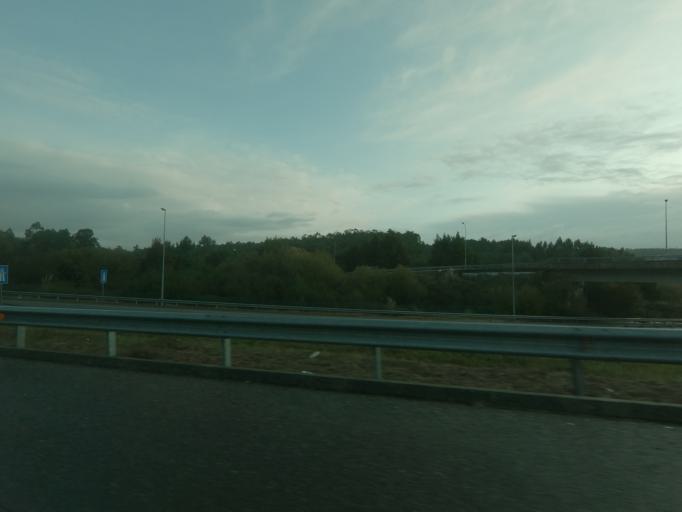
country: ES
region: Galicia
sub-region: Provincia de Pontevedra
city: Tui
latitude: 42.0677
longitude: -8.6392
